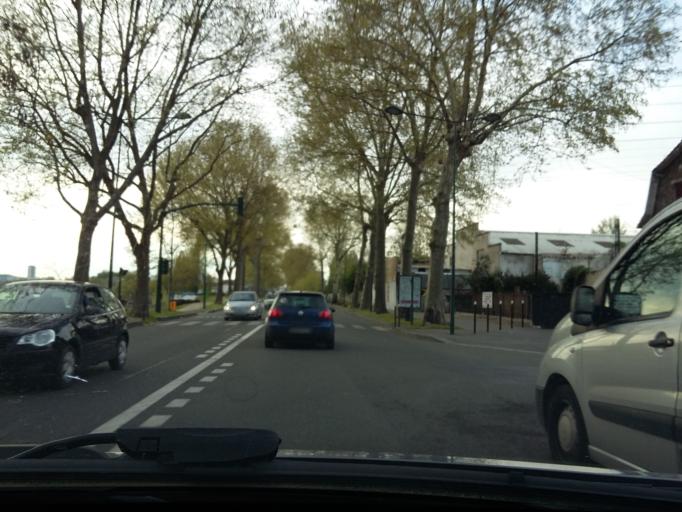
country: FR
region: Ile-de-France
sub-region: Departement de Seine-Saint-Denis
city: Villetaneuse
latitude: 48.9439
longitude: 2.3383
